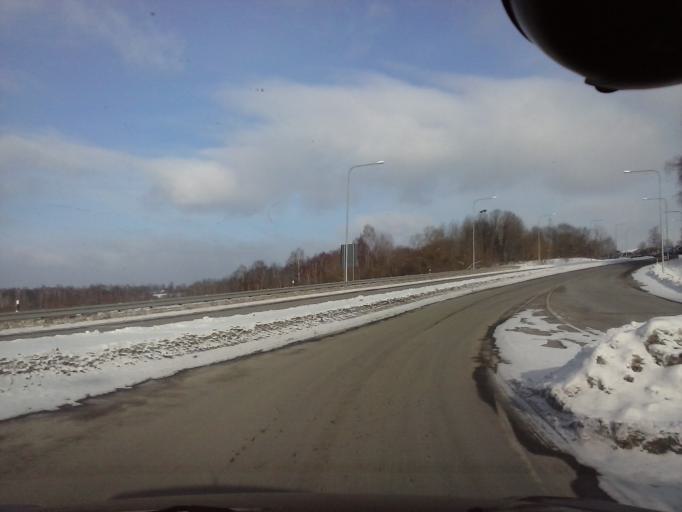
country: EE
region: Viljandimaa
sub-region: Viiratsi vald
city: Viiratsi
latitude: 58.3626
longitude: 25.6353
